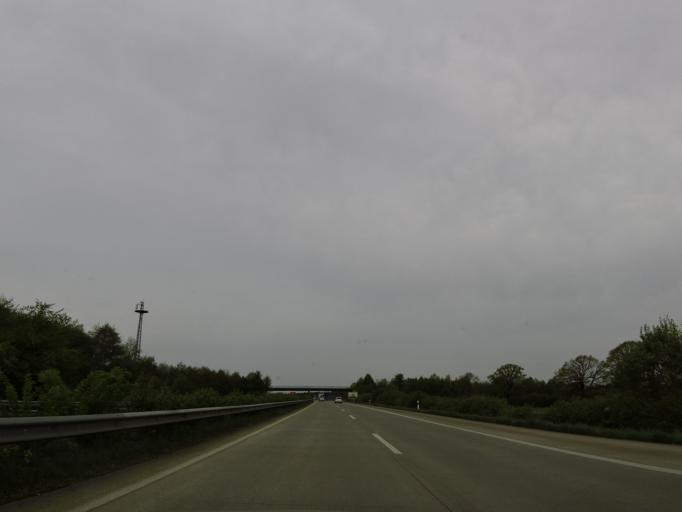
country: DE
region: Schleswig-Holstein
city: Dageling
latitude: 53.8865
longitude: 9.5390
